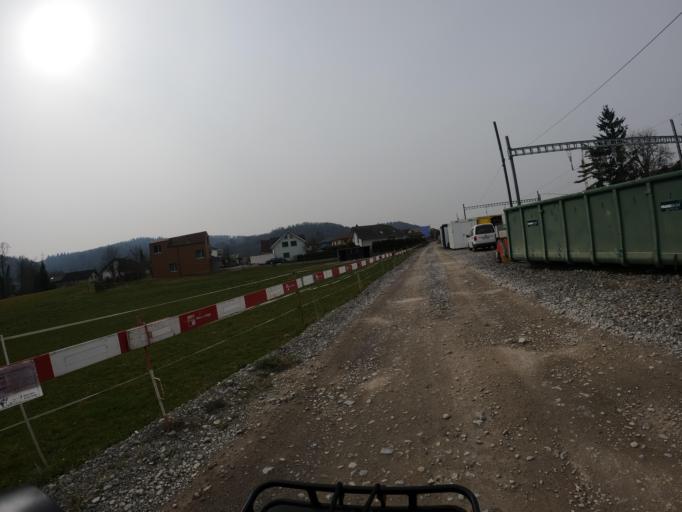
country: CH
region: Aargau
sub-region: Bezirk Lenzburg
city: Othmarsingen
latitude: 47.4166
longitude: 8.2404
